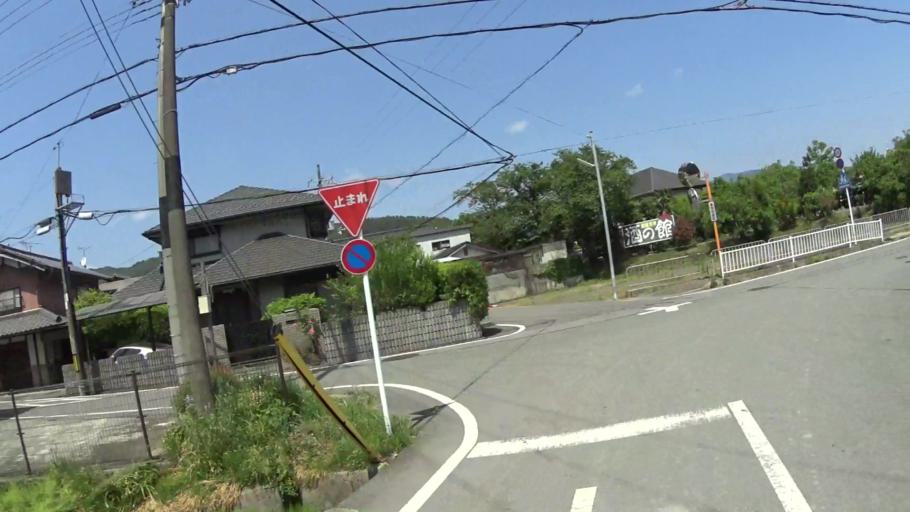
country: JP
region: Kyoto
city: Kameoka
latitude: 35.0182
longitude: 135.5315
